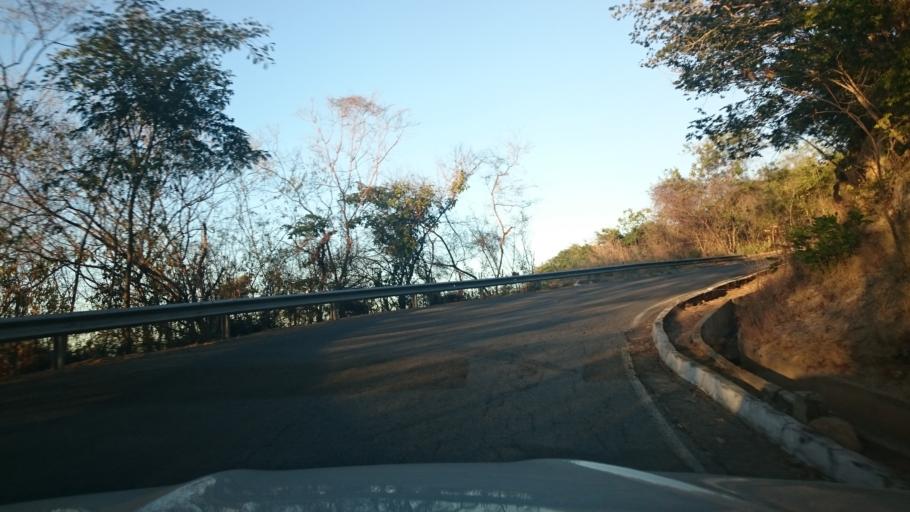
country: BR
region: Rio Grande do Norte
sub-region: Umarizal
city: Umarizal
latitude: -6.0188
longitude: -37.9886
